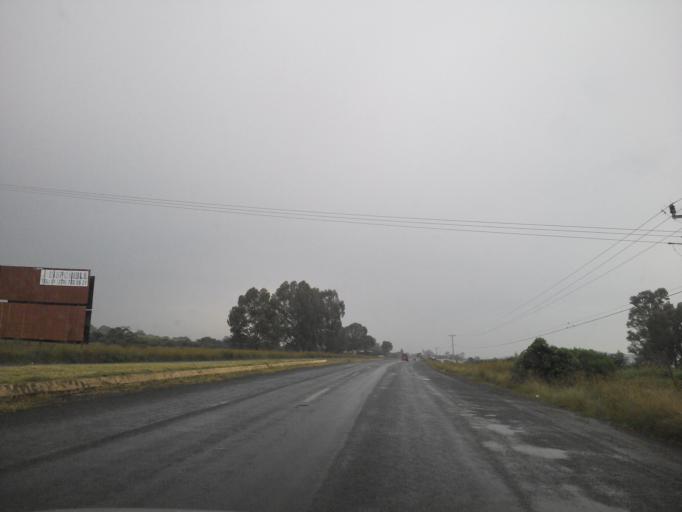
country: MX
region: Jalisco
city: Capilla de Guadalupe
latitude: 20.8423
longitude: -102.6090
